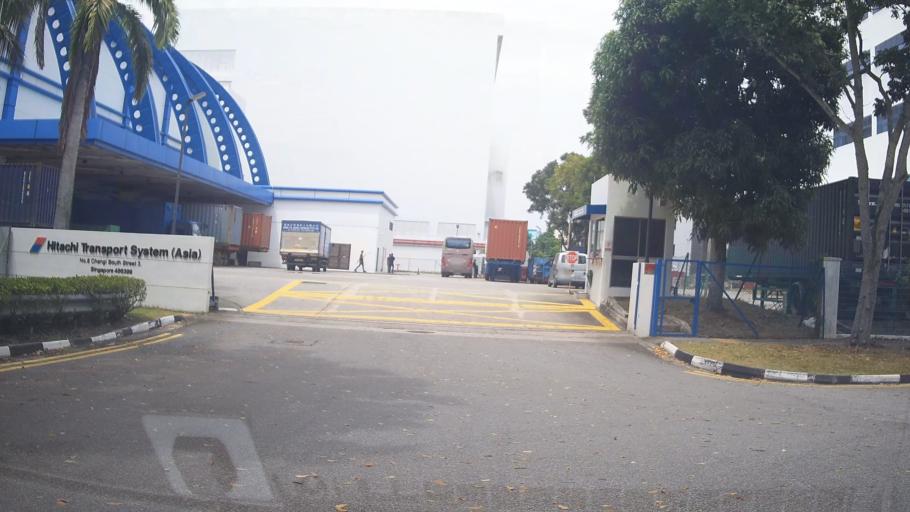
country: SG
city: Singapore
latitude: 1.3293
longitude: 103.9662
